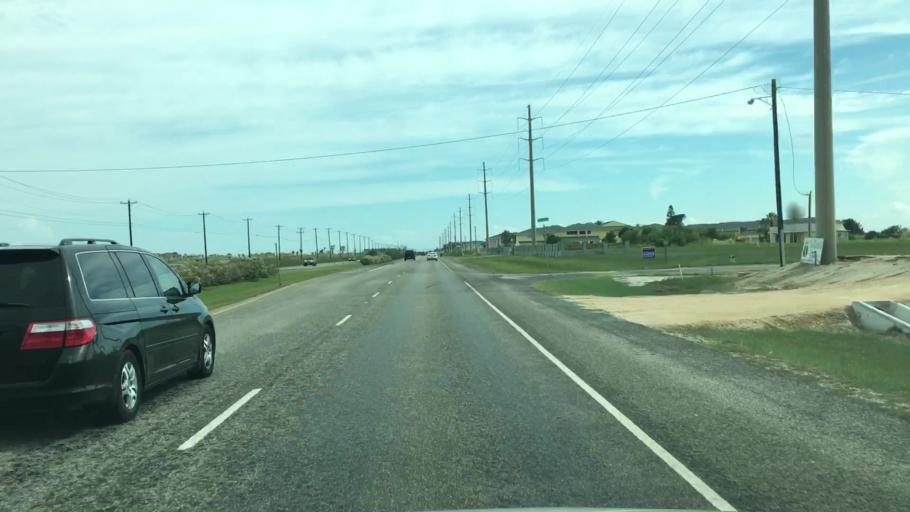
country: US
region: Texas
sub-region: Nueces County
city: Corpus Christi
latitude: 27.6148
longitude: -97.2223
